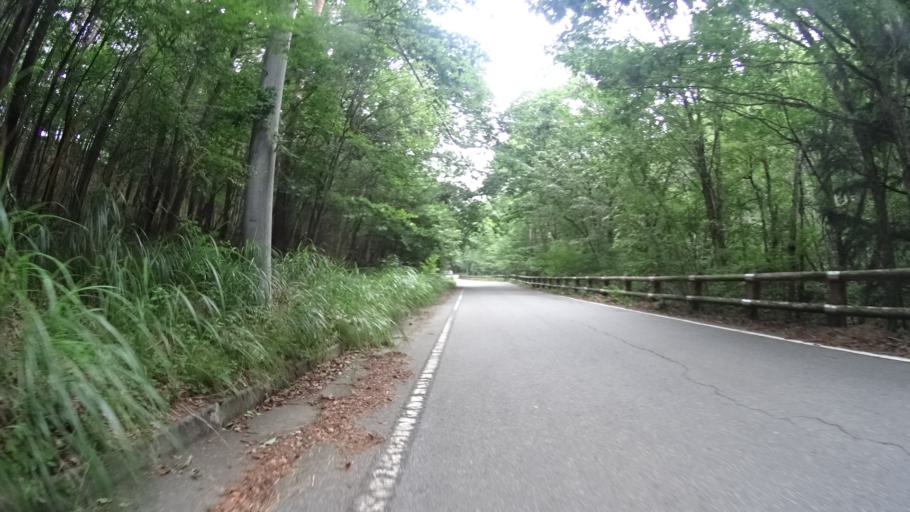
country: JP
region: Yamanashi
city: Nirasaki
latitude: 35.8913
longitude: 138.5658
